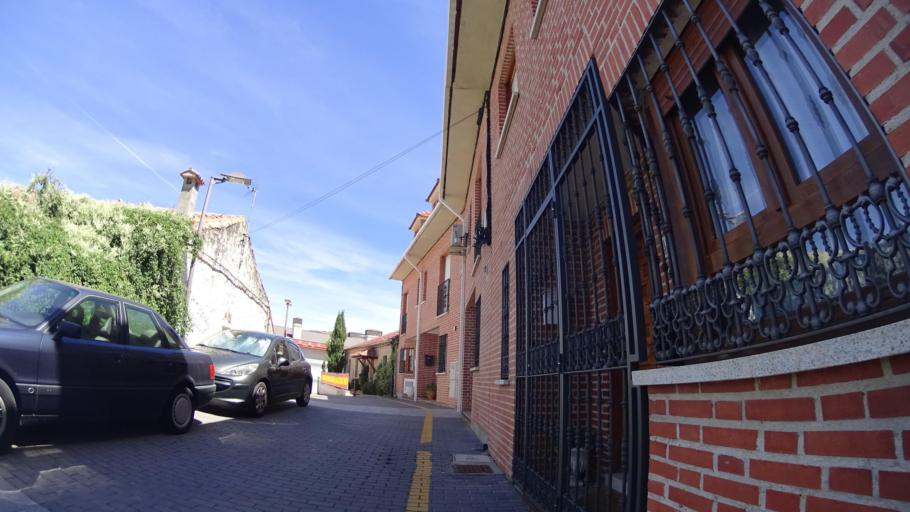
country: ES
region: Madrid
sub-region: Provincia de Madrid
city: Collado-Villalba
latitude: 40.6461
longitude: -3.9915
